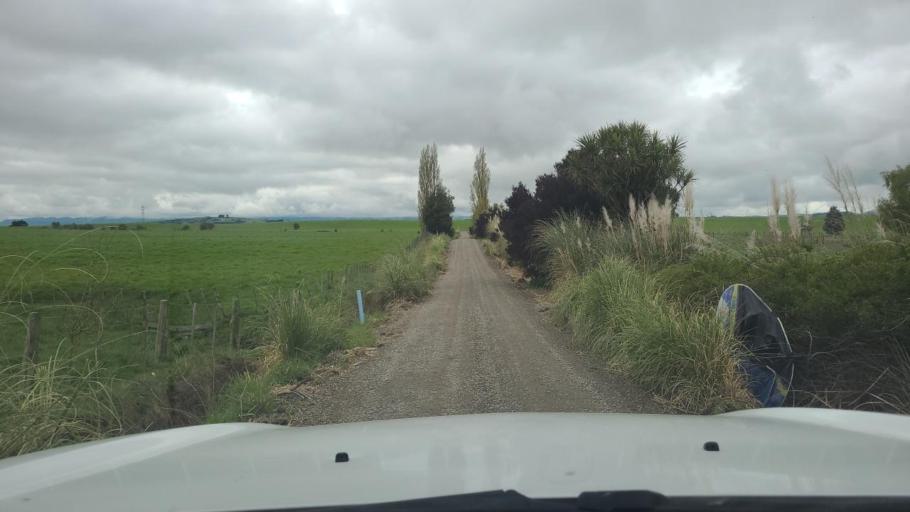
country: NZ
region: Wellington
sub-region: Masterton District
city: Masterton
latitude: -41.0465
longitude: 175.5219
